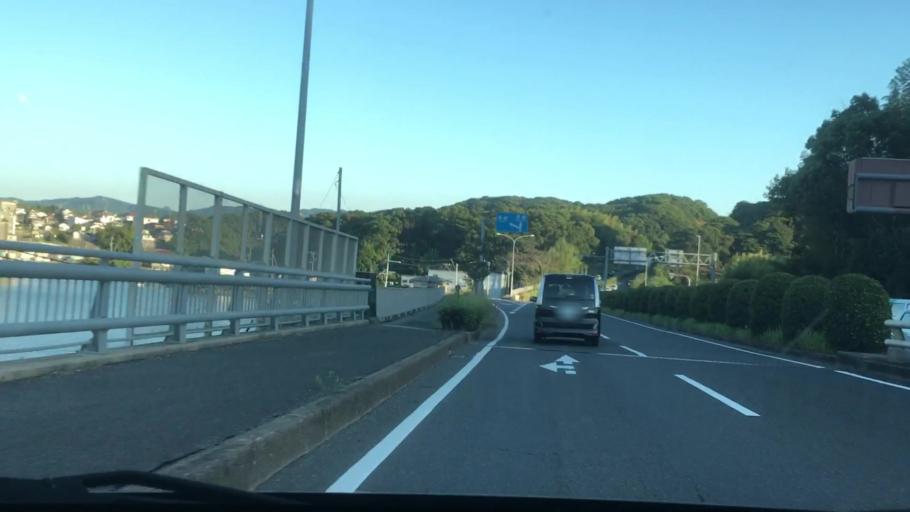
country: JP
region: Nagasaki
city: Sasebo
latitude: 33.1415
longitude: 129.7826
